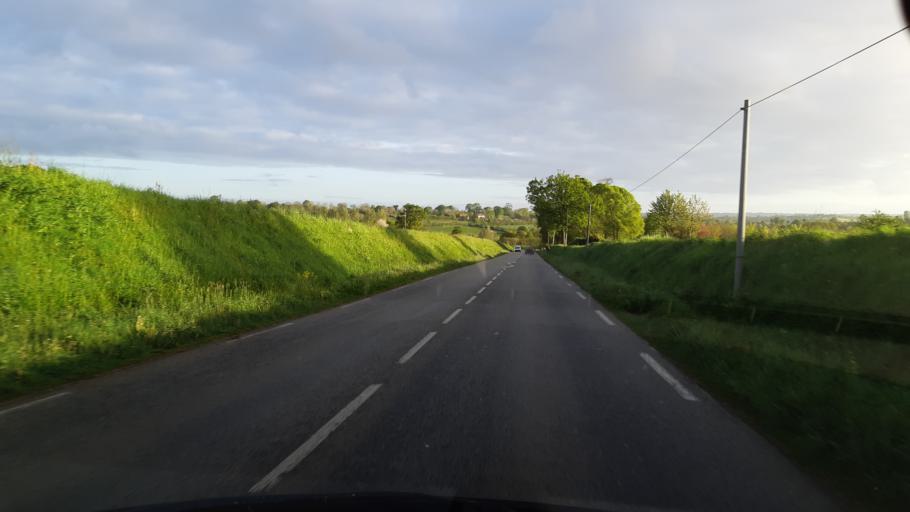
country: FR
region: Lower Normandy
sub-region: Departement de la Manche
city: Agneaux
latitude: 49.0621
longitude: -1.1329
